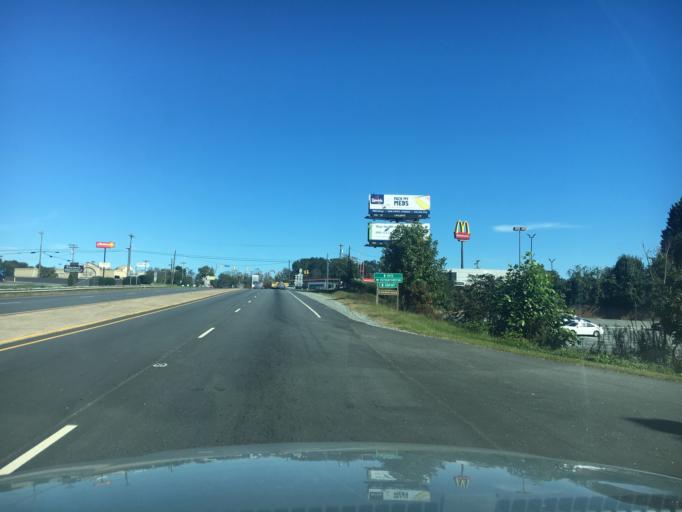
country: US
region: North Carolina
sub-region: Rutherford County
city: Spindale
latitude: 35.3612
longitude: -81.9424
